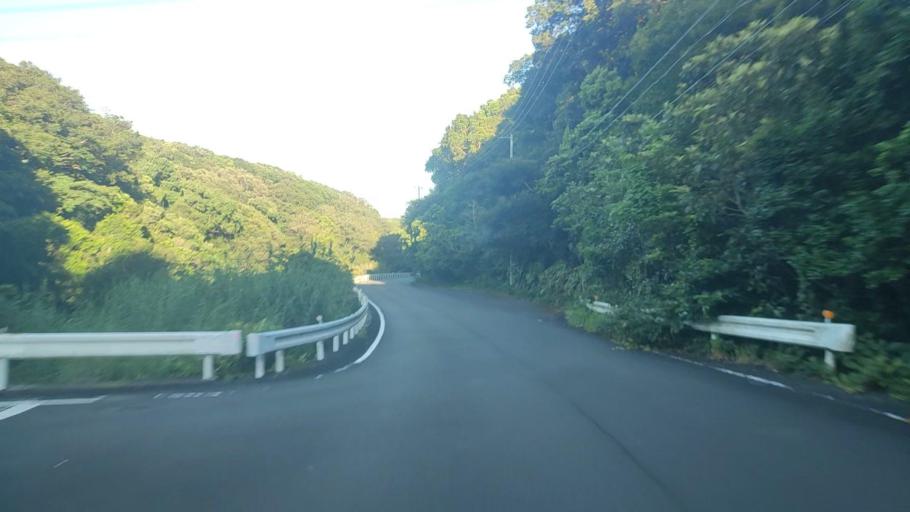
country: JP
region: Mie
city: Toba
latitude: 34.2635
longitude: 136.7728
